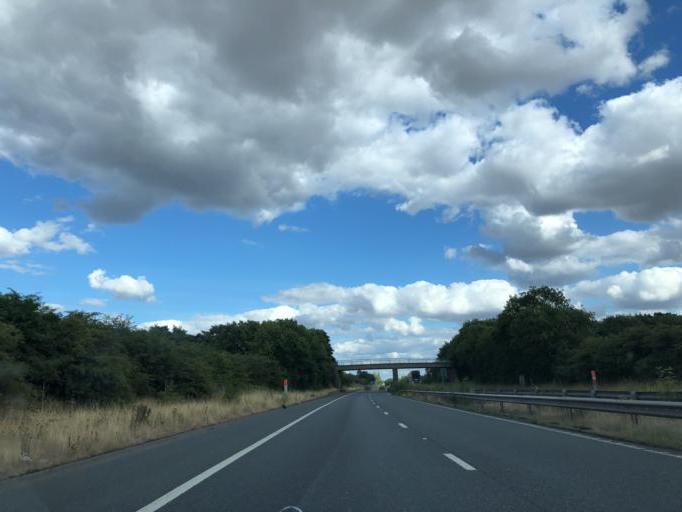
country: GB
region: England
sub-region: Warwickshire
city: Dunchurch
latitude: 52.3391
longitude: -1.3157
